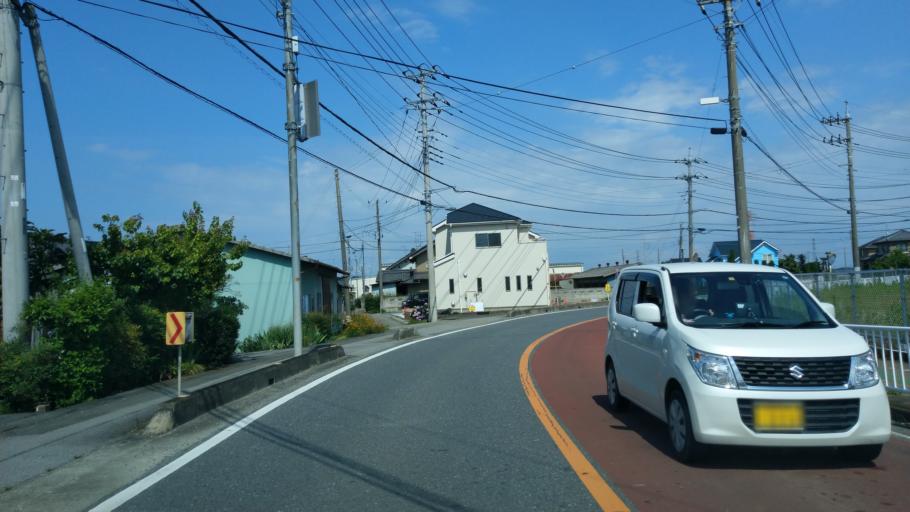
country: JP
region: Saitama
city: Kodamacho-kodamaminami
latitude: 36.2099
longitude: 139.1510
